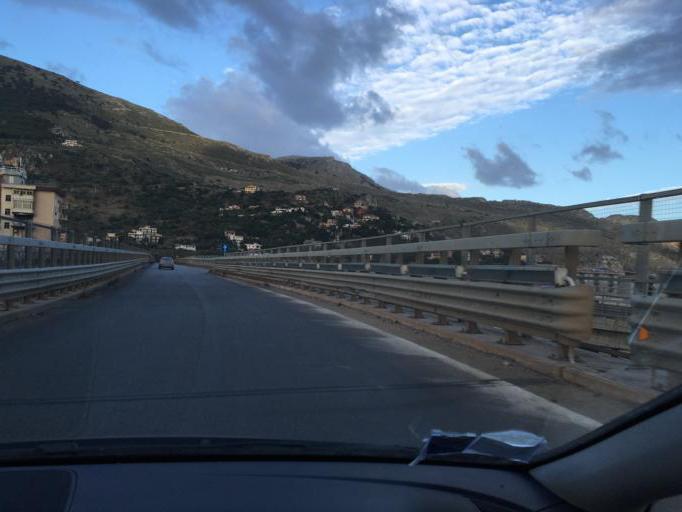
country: IT
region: Sicily
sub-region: Palermo
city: Isola delle Femmine
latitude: 38.1925
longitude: 13.2870
